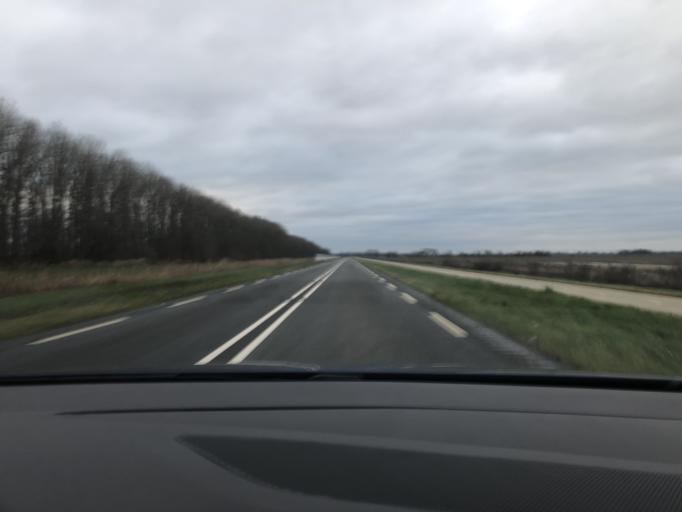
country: NL
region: Flevoland
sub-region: Gemeente Lelystad
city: Lelystad
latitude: 52.4609
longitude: 5.5118
